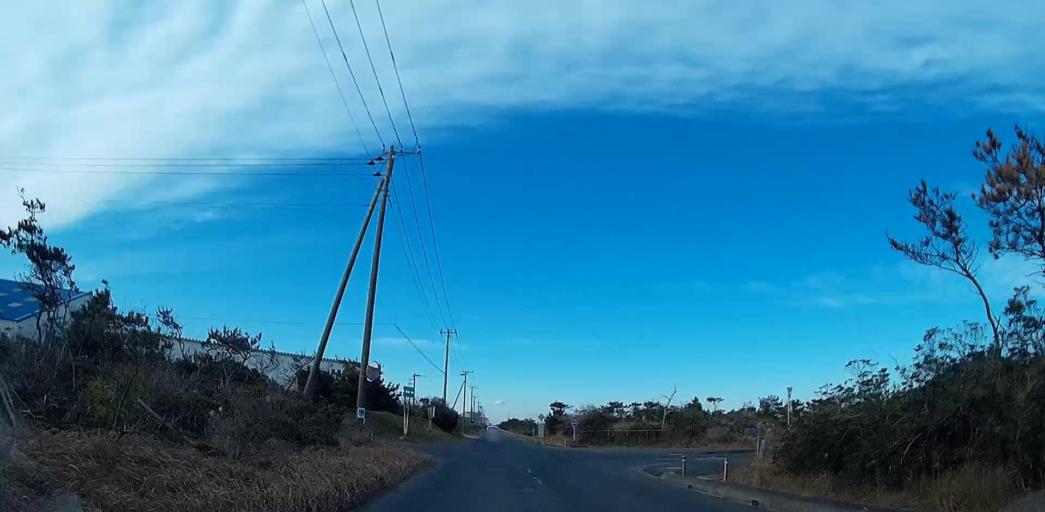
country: JP
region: Chiba
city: Hasaki
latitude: 35.7580
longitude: 140.8249
